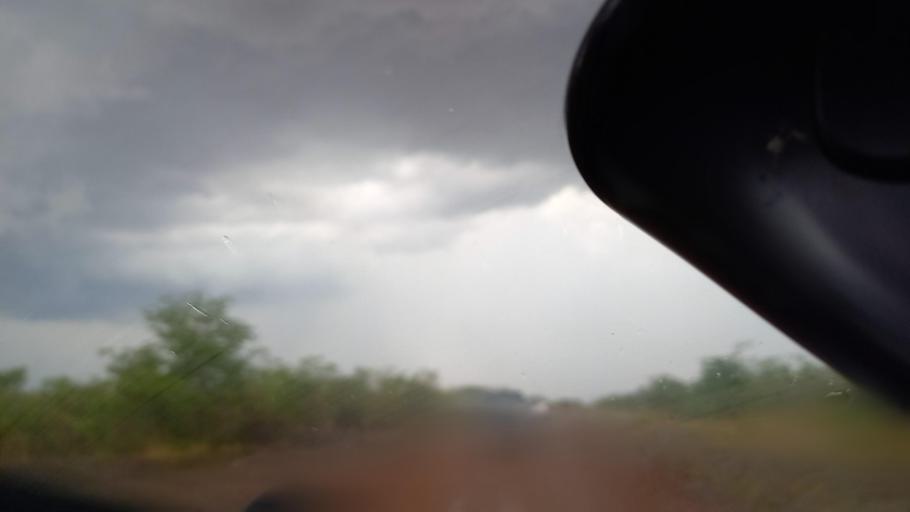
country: ZM
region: Lusaka
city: Kafue
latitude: -15.8650
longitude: 28.1800
